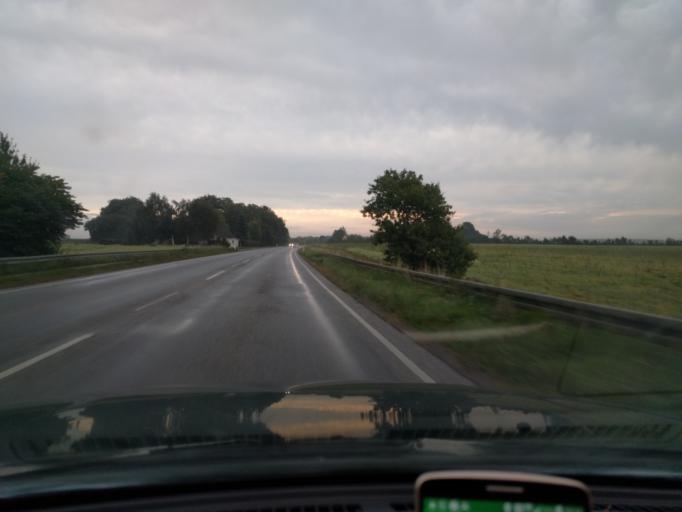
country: DK
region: Zealand
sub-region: Guldborgsund Kommune
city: Norre Alslev
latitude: 54.8996
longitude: 11.9053
